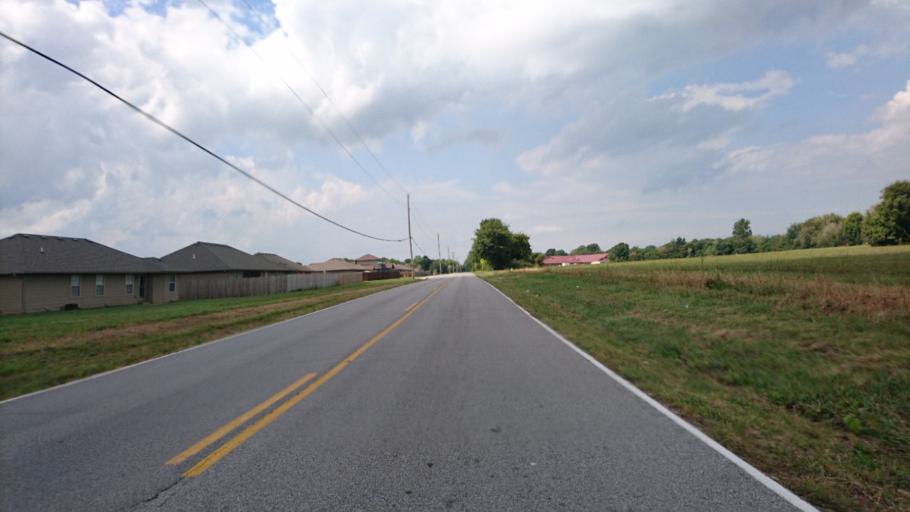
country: US
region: Missouri
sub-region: Greene County
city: Springfield
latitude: 37.1977
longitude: -93.3666
